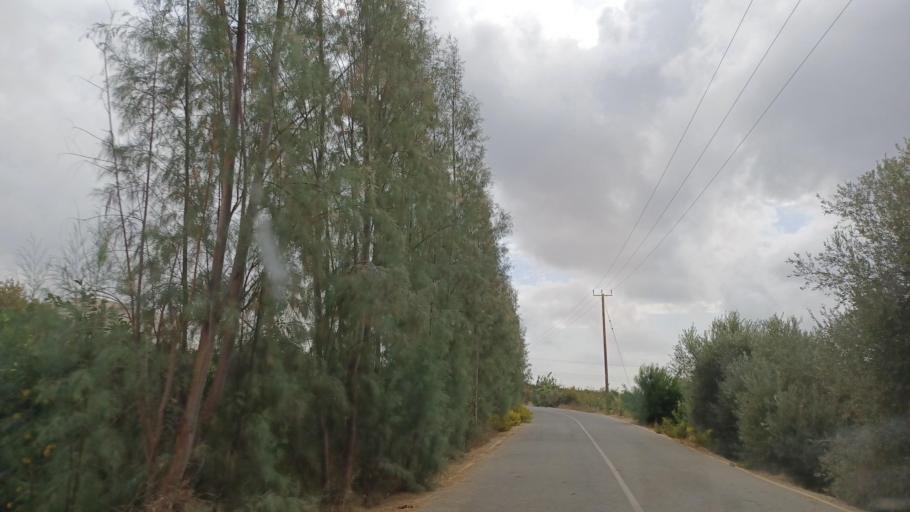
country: CY
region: Pafos
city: Kissonerga
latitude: 34.8301
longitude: 32.4143
